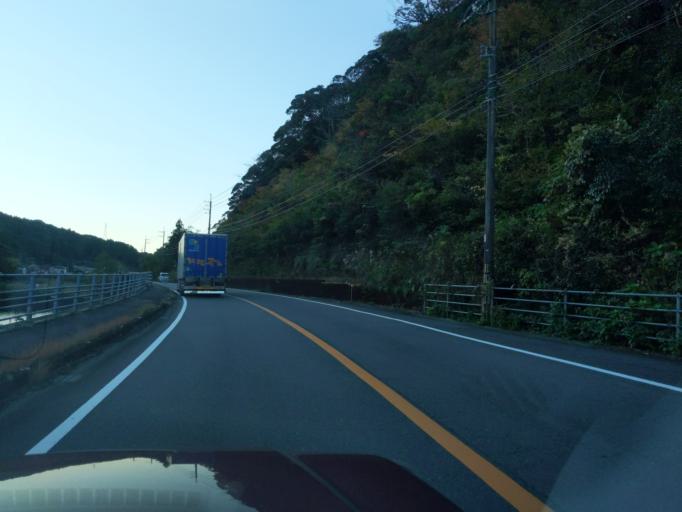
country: JP
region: Tokushima
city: Anan
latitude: 33.6837
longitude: 134.4206
